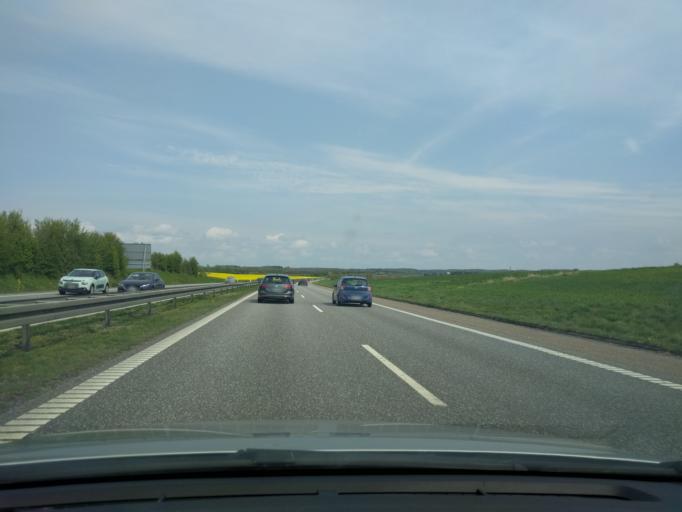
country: DK
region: Zealand
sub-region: Slagelse Kommune
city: Slagelse
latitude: 55.4266
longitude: 11.4301
